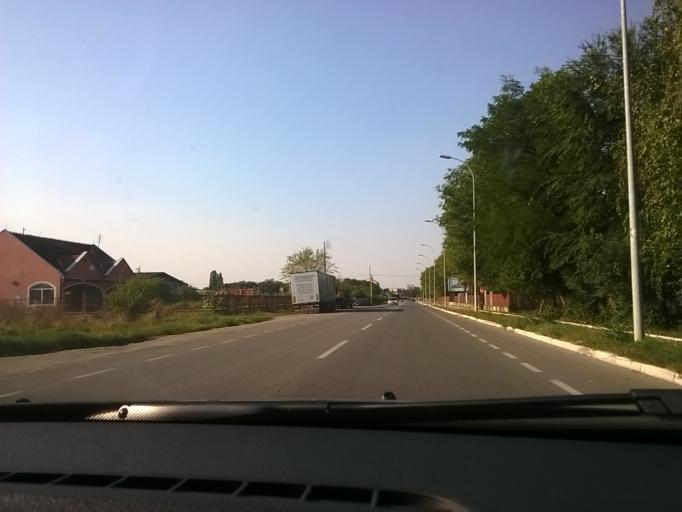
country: RS
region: Autonomna Pokrajina Vojvodina
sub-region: Juznobanatski Okrug
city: Vrsac
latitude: 45.1292
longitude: 21.2882
